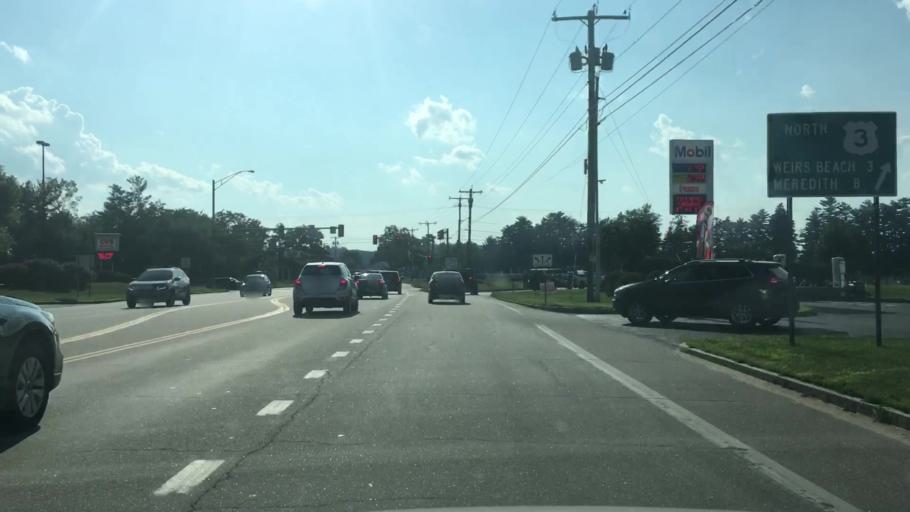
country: US
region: New Hampshire
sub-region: Belknap County
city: Laconia
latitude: 43.5629
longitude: -71.4474
